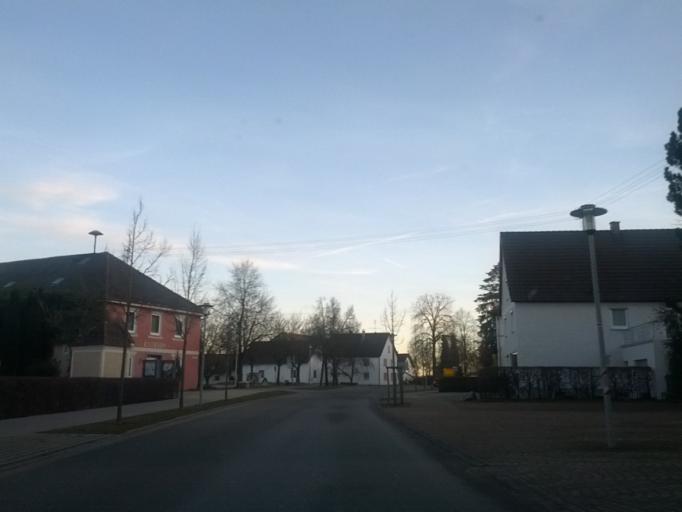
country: DE
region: Baden-Wuerttemberg
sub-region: Tuebingen Region
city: Berkheim
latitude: 48.0403
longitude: 10.0834
